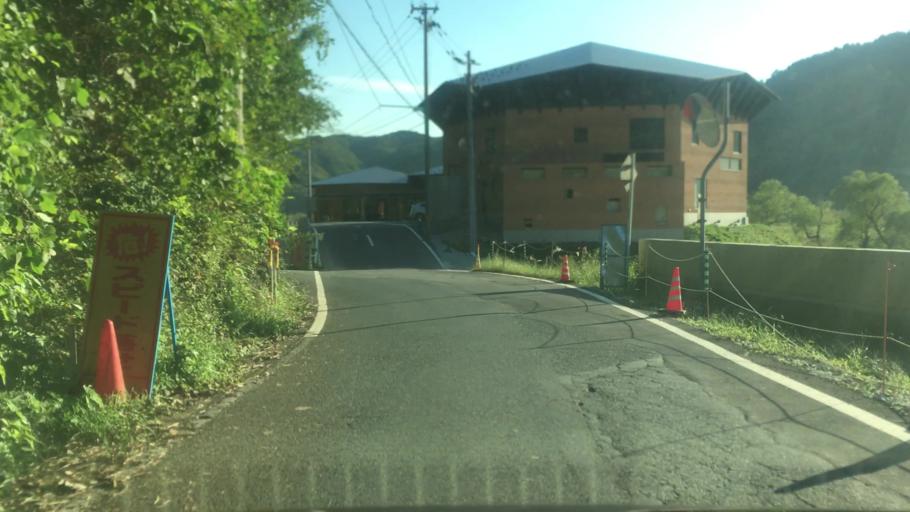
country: JP
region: Hyogo
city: Toyooka
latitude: 35.5899
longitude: 134.8038
